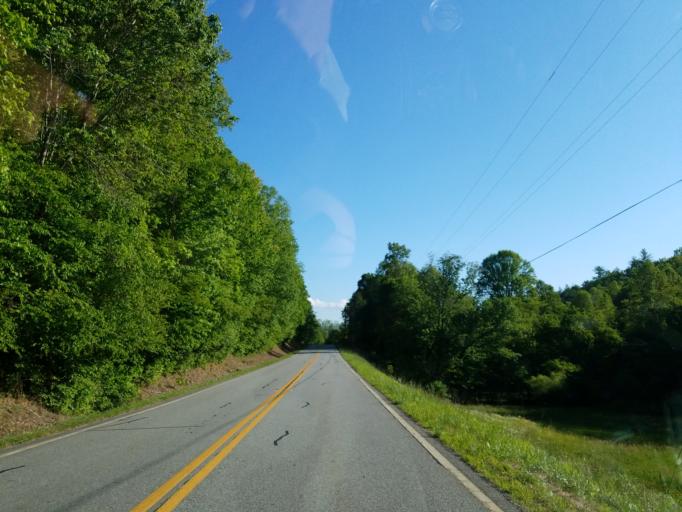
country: US
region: Georgia
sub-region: Fannin County
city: Blue Ridge
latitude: 34.7861
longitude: -84.1842
